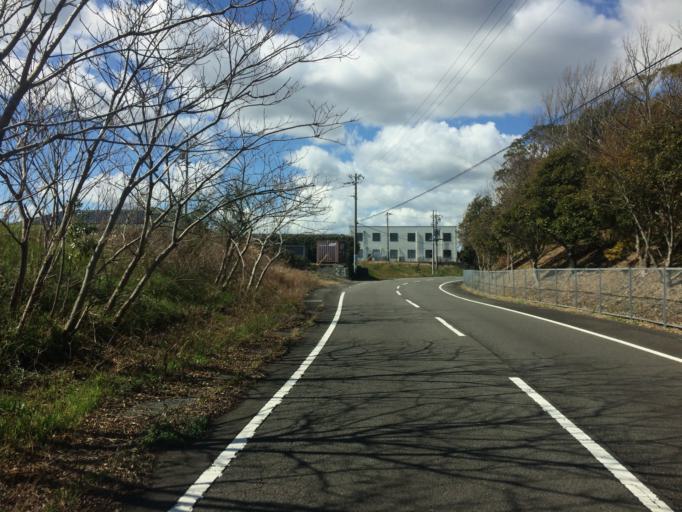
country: JP
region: Shizuoka
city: Shimada
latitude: 34.7573
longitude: 138.1629
